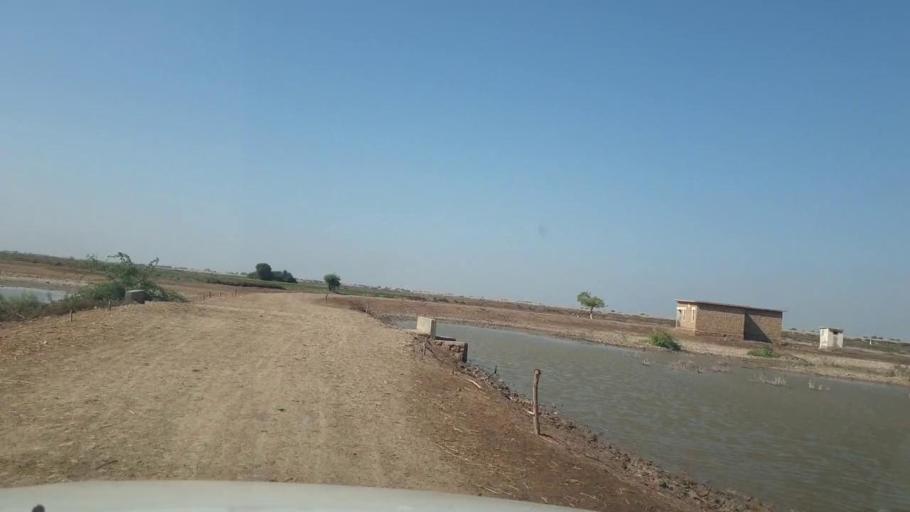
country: PK
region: Sindh
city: Chuhar Jamali
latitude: 24.4374
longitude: 67.8415
